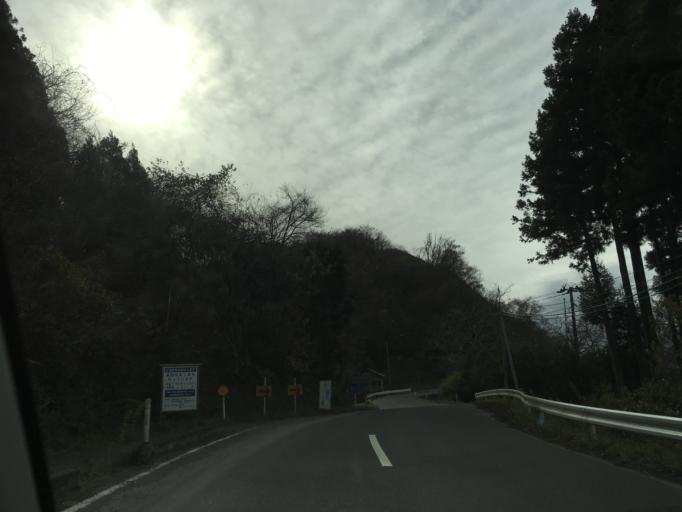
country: JP
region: Iwate
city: Ichinoseki
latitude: 38.7507
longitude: 141.2858
